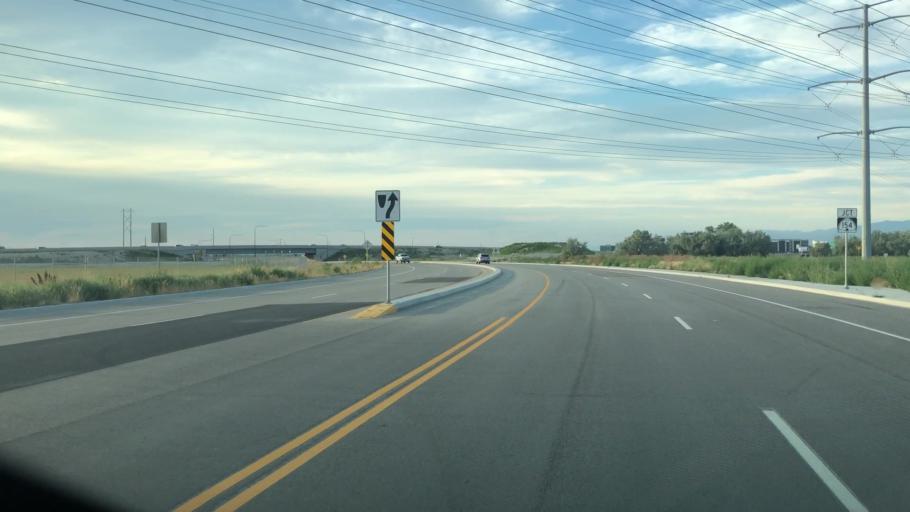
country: US
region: Utah
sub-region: Salt Lake County
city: Bluffdale
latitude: 40.4973
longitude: -111.9055
